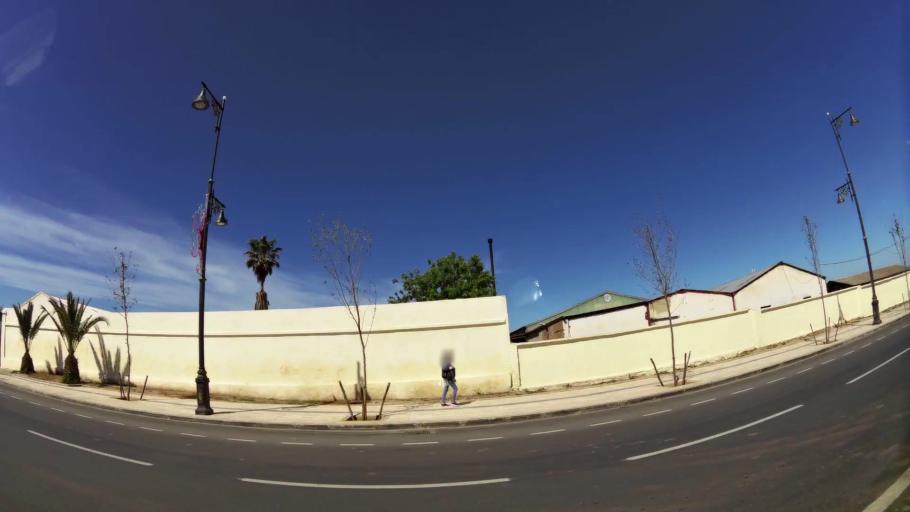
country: MA
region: Meknes-Tafilalet
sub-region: Meknes
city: Meknes
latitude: 33.8486
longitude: -5.5249
